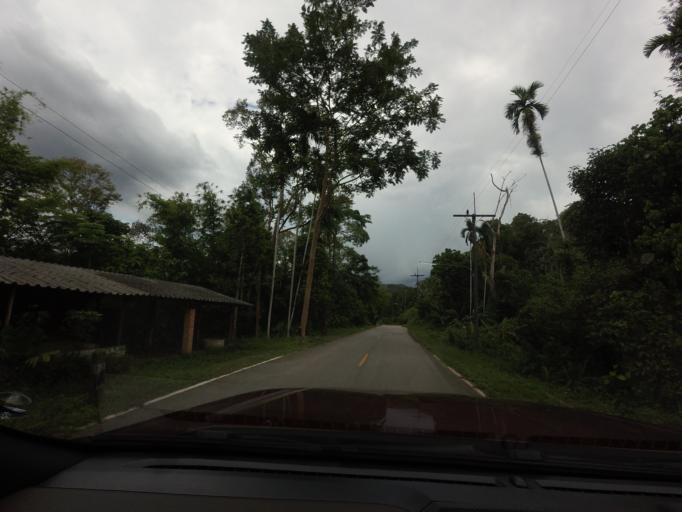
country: TH
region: Narathiwat
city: Sukhirin
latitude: 5.9869
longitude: 101.7061
